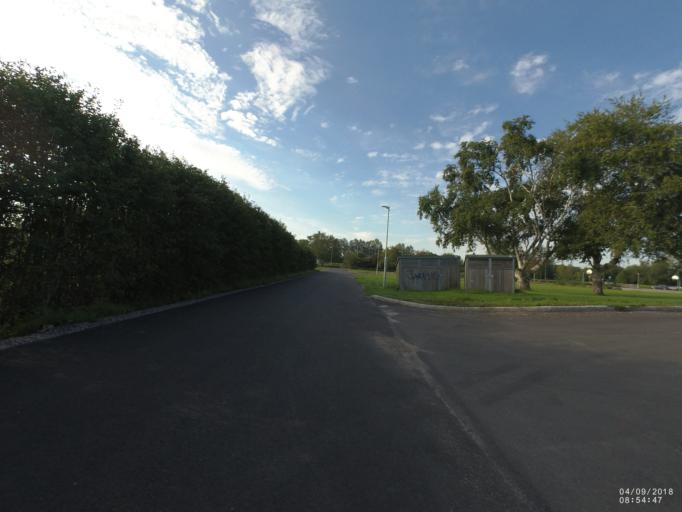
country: SE
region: Soedermanland
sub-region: Nykopings Kommun
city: Nykoping
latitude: 58.7512
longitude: 16.9862
